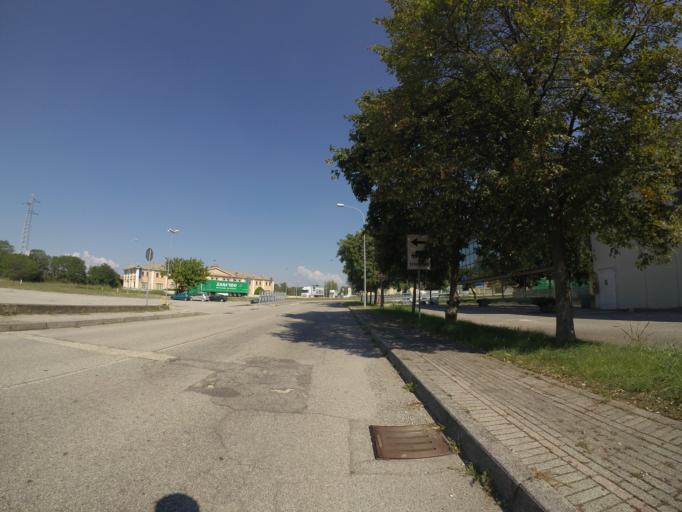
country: IT
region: Friuli Venezia Giulia
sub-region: Provincia di Udine
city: Codroipo
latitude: 45.9712
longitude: 12.9858
